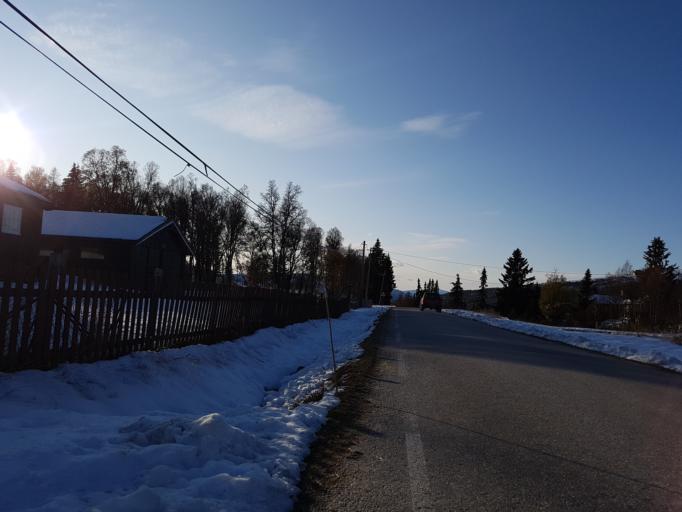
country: NO
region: Oppland
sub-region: Sel
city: Otta
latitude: 61.8091
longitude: 9.6807
